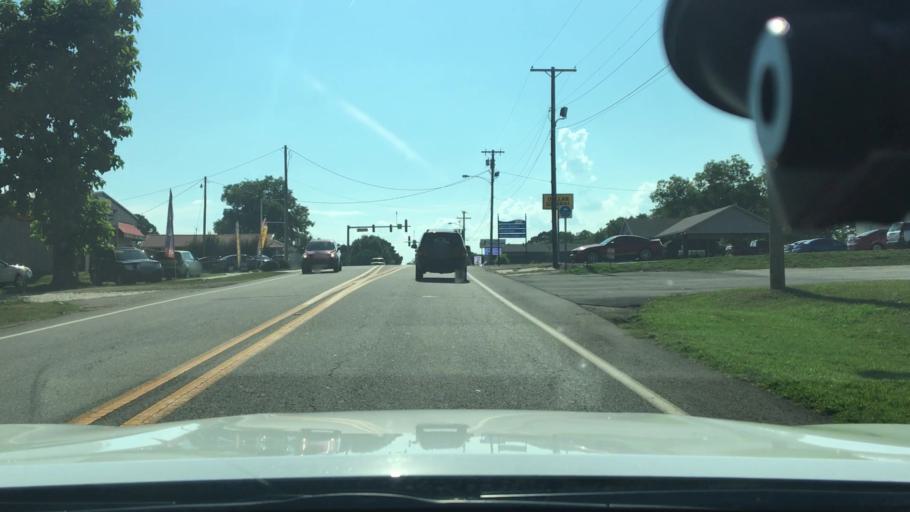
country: US
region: Arkansas
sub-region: Johnson County
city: Clarksville
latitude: 35.4715
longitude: -93.4773
